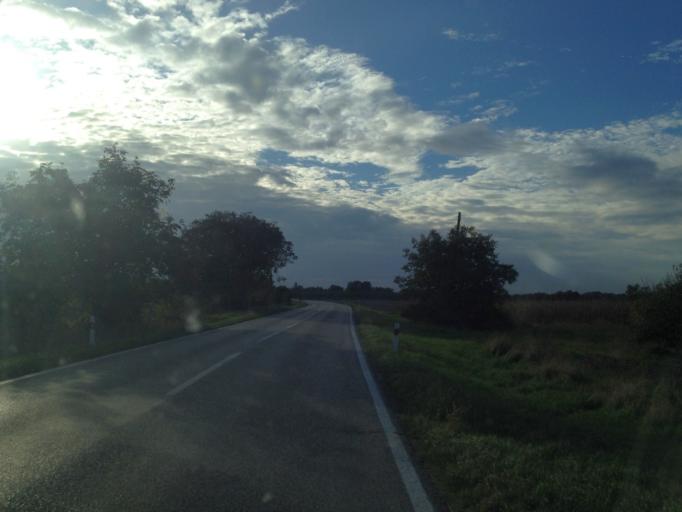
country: HU
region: Komarom-Esztergom
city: Dunaalmas
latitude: 47.7403
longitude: 18.3005
